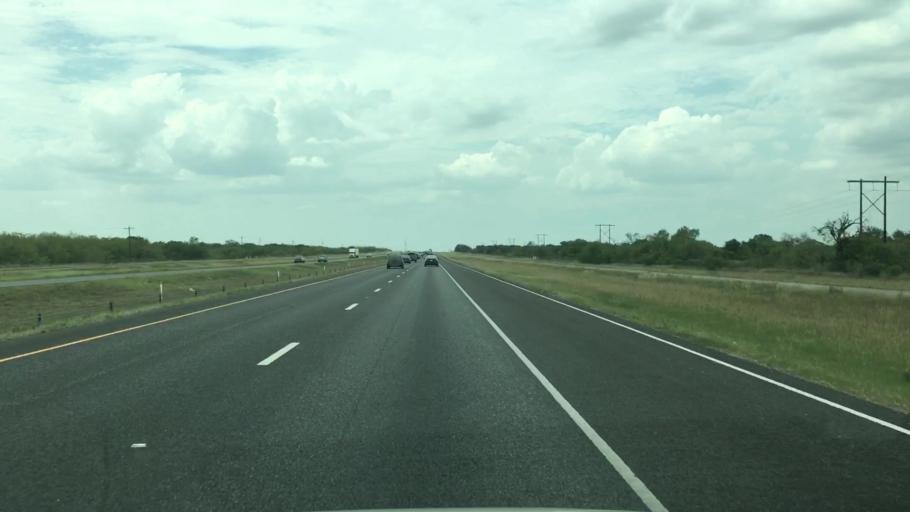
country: US
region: Texas
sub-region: Atascosa County
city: Pleasanton
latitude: 28.8060
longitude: -98.3469
